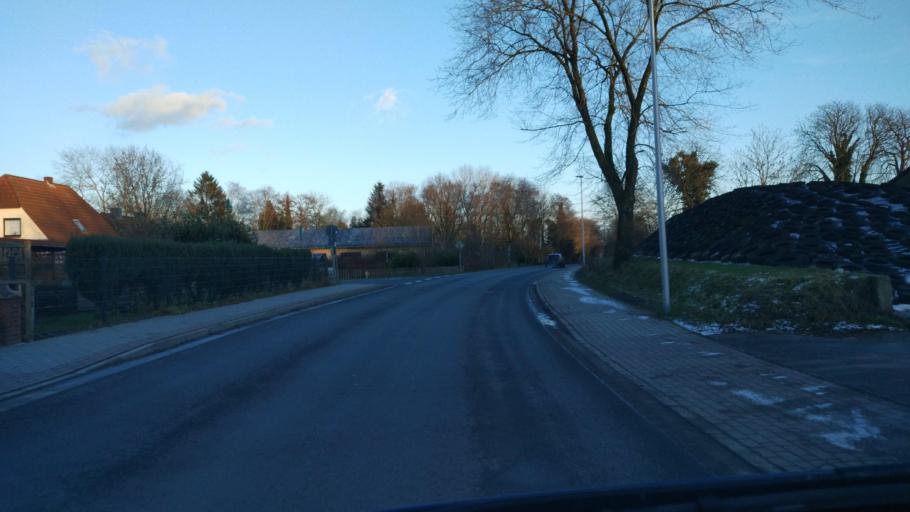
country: DE
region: Schleswig-Holstein
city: Ostenfeld
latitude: 54.4609
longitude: 9.2445
